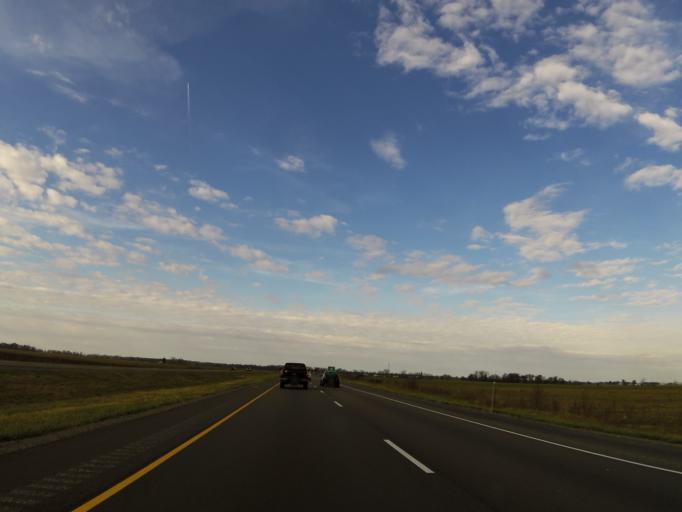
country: US
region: Illinois
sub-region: Washington County
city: Okawville
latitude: 38.4315
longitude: -89.5064
